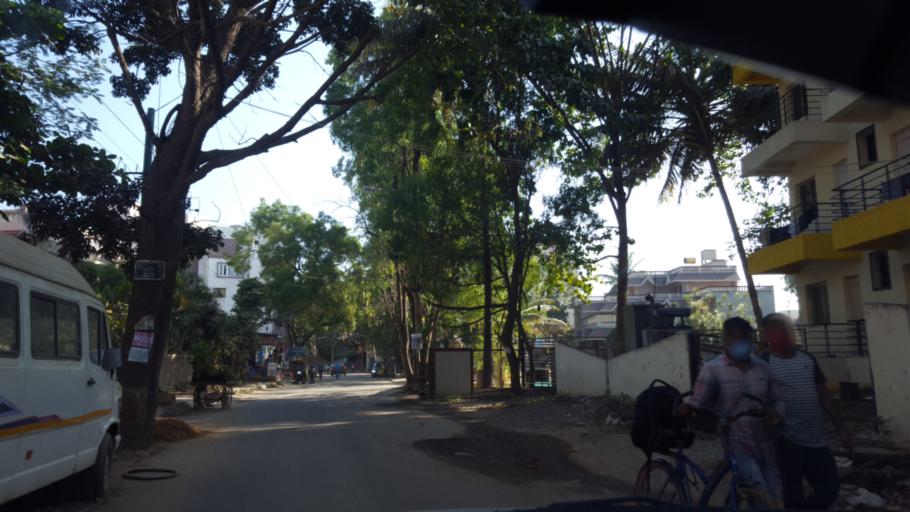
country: IN
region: Karnataka
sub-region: Bangalore Urban
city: Bangalore
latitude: 12.9534
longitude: 77.7055
